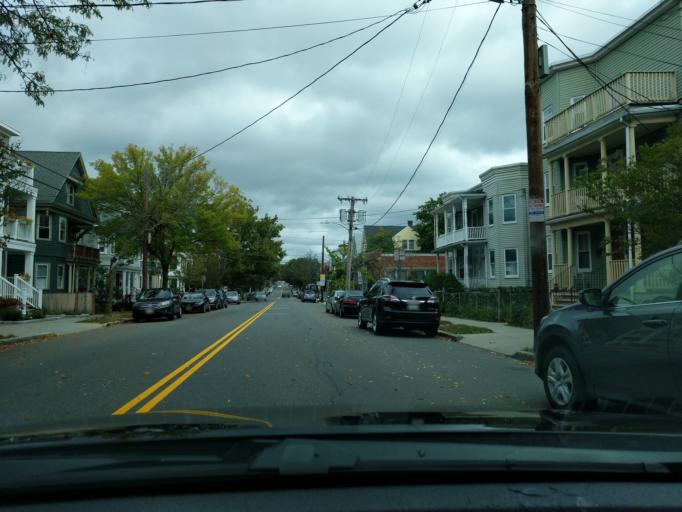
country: US
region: Massachusetts
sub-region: Middlesex County
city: Medford
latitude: 42.3982
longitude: -71.1294
